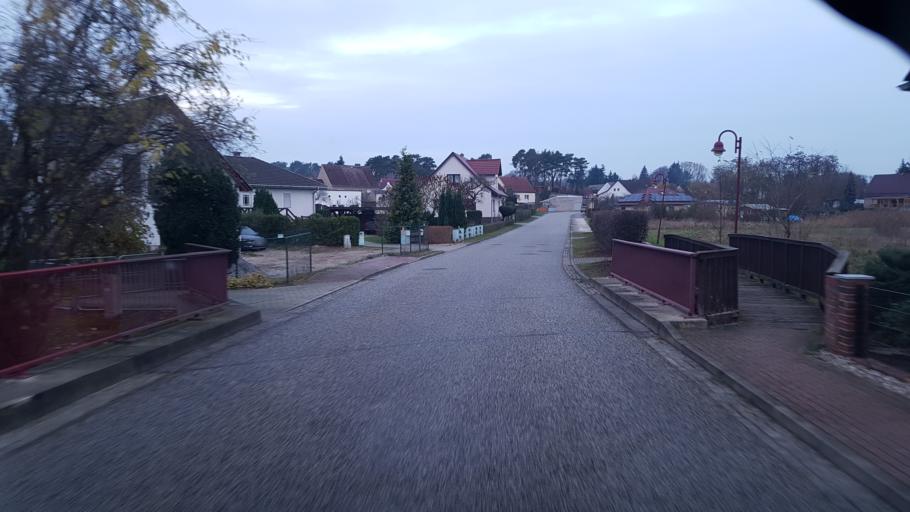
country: DE
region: Brandenburg
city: Gross Lindow
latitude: 52.1867
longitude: 14.5346
